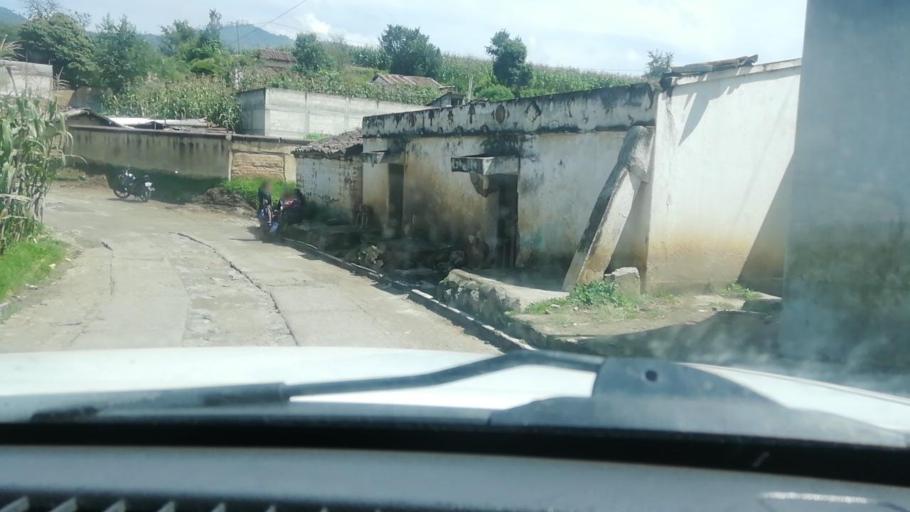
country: GT
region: Totonicapan
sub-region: Municipio de San Andres Xecul
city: San Andres Xecul
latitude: 14.8913
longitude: -91.4734
